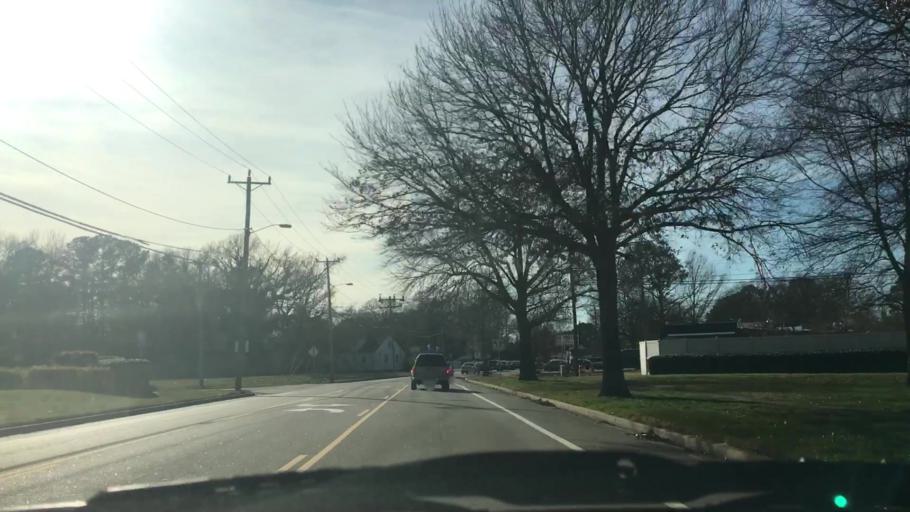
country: US
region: Virginia
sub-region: City of Norfolk
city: Norfolk
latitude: 36.8794
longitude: -76.2250
